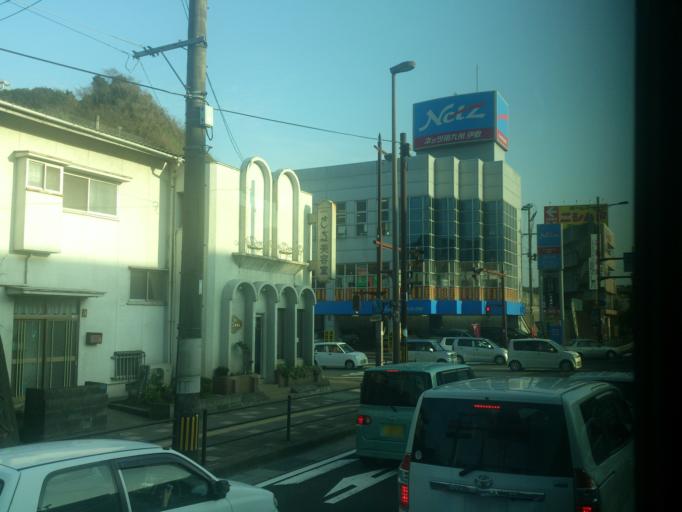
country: JP
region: Kagoshima
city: Kagoshima-shi
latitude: 31.6226
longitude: 130.5267
